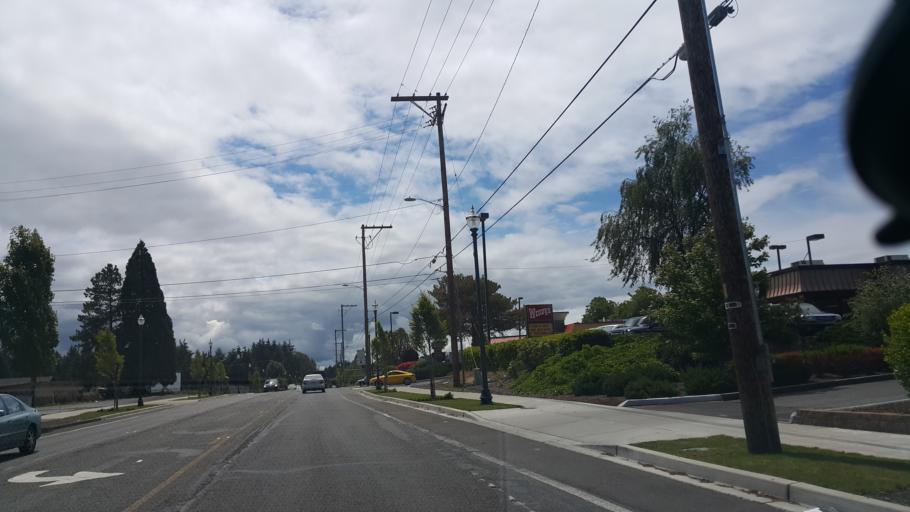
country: US
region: Washington
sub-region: Pierce County
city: Fircrest
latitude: 47.2413
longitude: -122.5264
